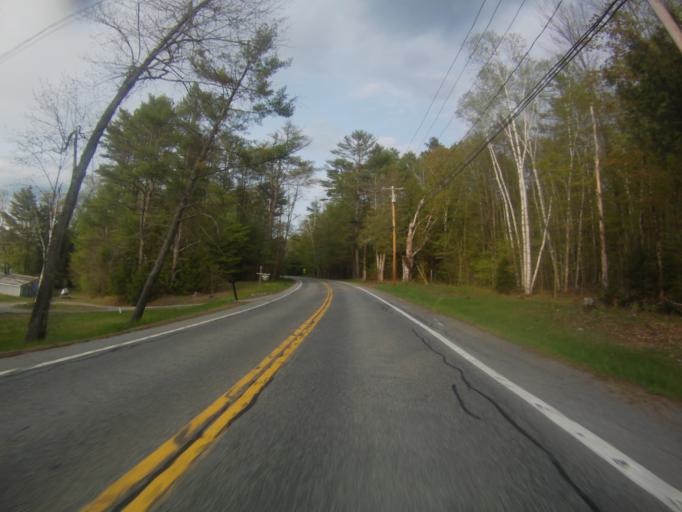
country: US
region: New York
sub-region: Warren County
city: Warrensburg
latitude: 43.7224
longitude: -73.6862
